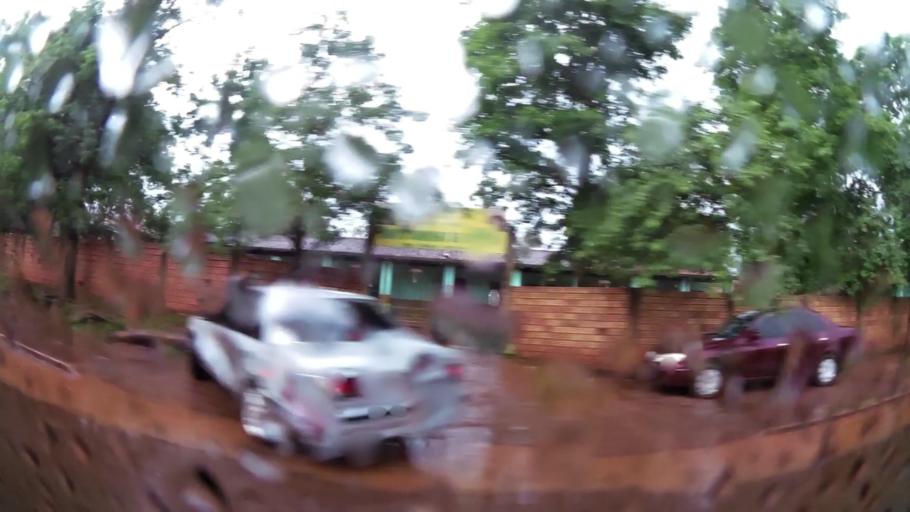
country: PY
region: Alto Parana
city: Presidente Franco
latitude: -25.5471
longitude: -54.6747
